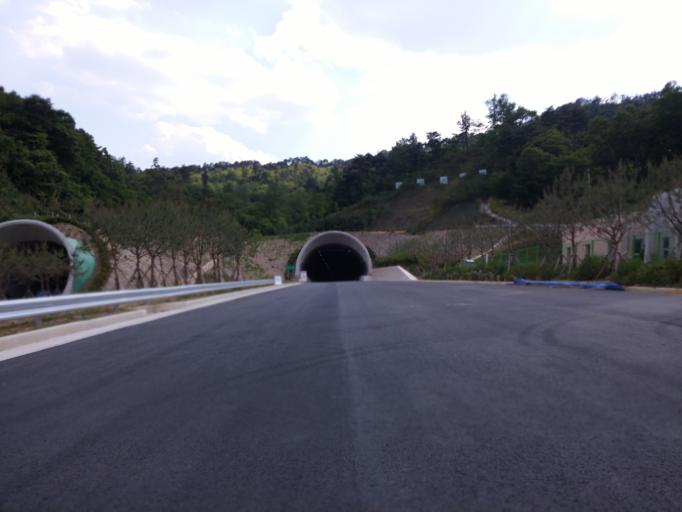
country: KR
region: Daejeon
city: Sintansin
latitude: 36.4985
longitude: 127.4683
